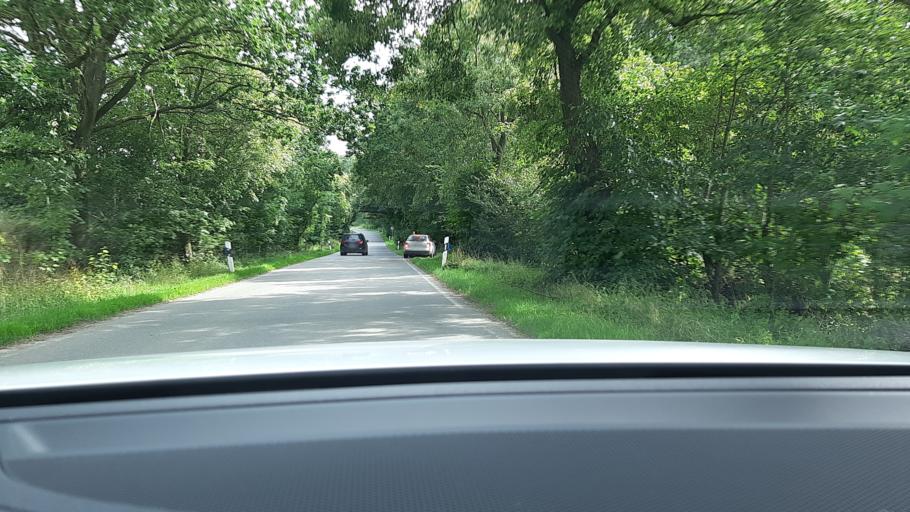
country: DE
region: Schleswig-Holstein
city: Rehhorst
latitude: 53.8581
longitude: 10.4654
